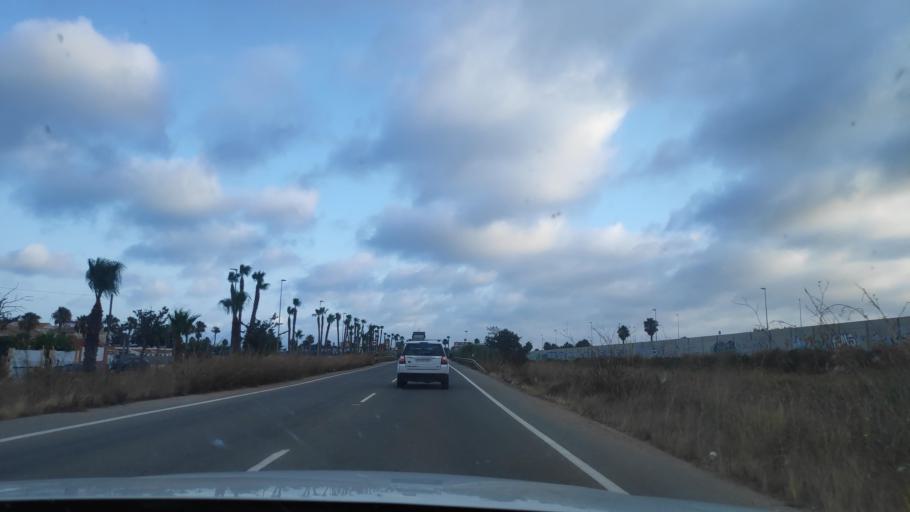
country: ES
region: Murcia
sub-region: Murcia
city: Los Alcazares
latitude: 37.7697
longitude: -0.8435
